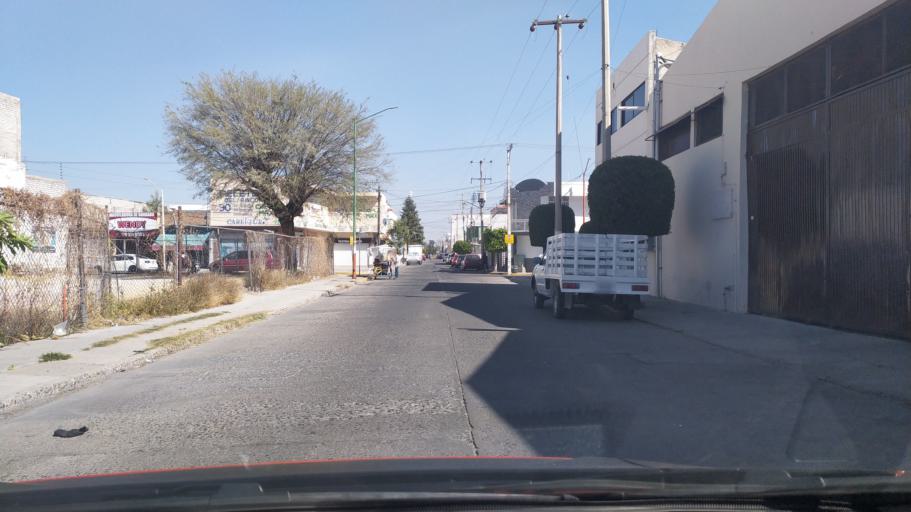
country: MX
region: Guanajuato
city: San Francisco del Rincon
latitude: 21.0242
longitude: -101.8539
